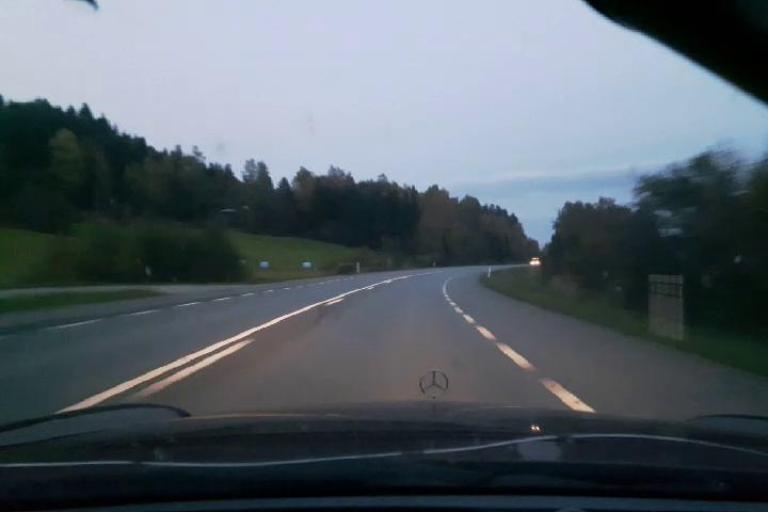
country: SE
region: Vaesternorrland
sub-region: Kramfors Kommun
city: Nordingra
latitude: 63.0075
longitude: 18.2804
